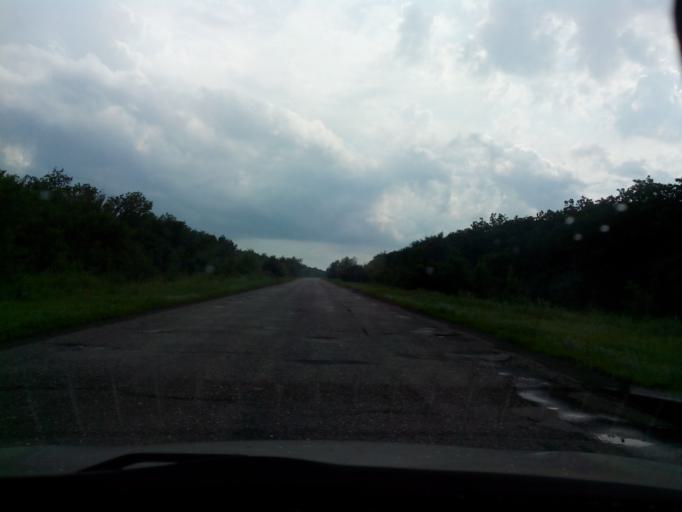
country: RU
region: Volgograd
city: Mikhaylovka
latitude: 49.9112
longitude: 42.9562
